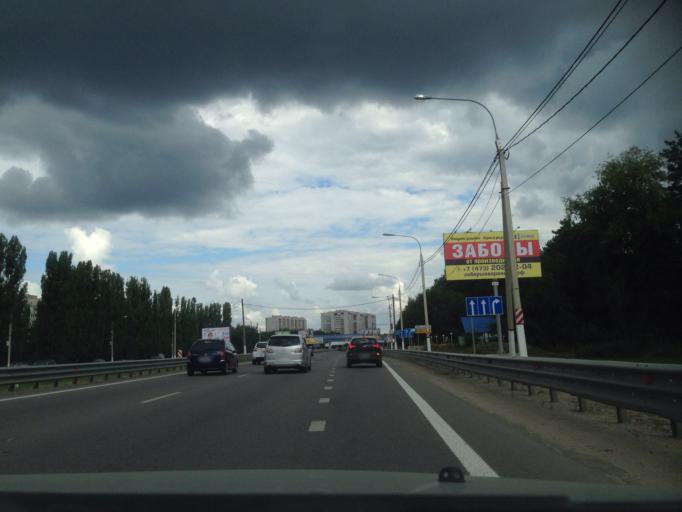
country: RU
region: Voronezj
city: Podgornoye
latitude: 51.7249
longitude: 39.1793
